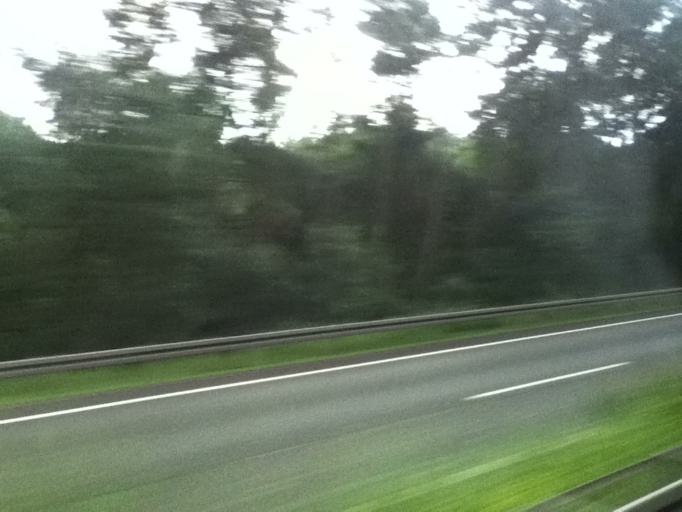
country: DE
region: Thuringia
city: Grossensee
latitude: 50.9463
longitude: 9.9625
